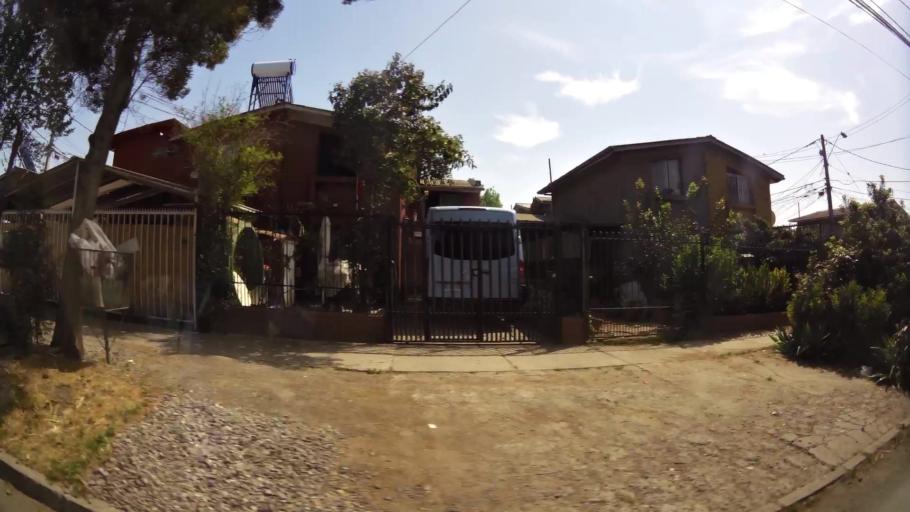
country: CL
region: Santiago Metropolitan
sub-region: Provincia de Santiago
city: Lo Prado
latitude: -33.4821
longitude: -70.7336
